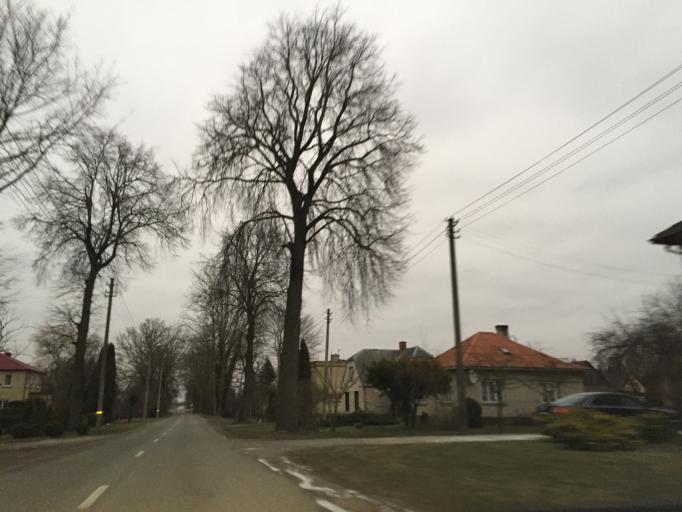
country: LT
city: Zagare
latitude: 56.3451
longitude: 23.3090
